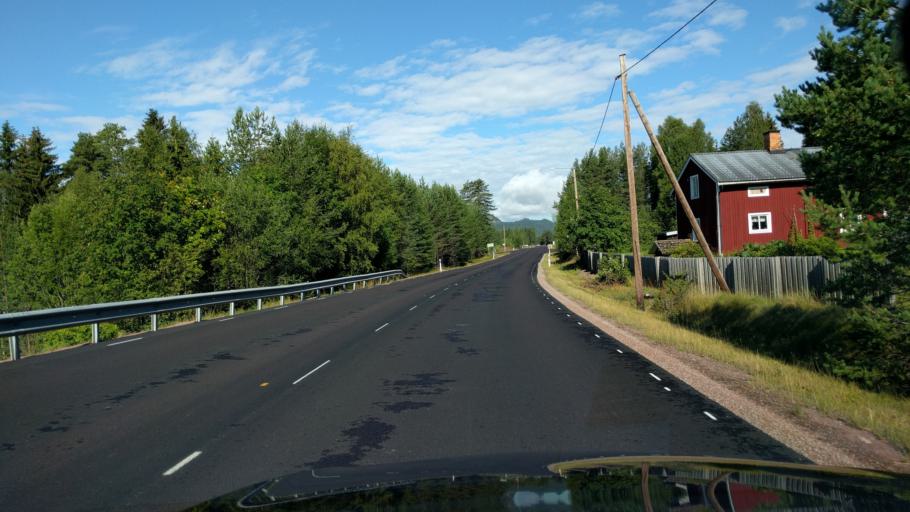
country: SE
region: Dalarna
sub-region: Alvdalens Kommun
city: AElvdalen
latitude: 61.1471
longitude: 14.1496
